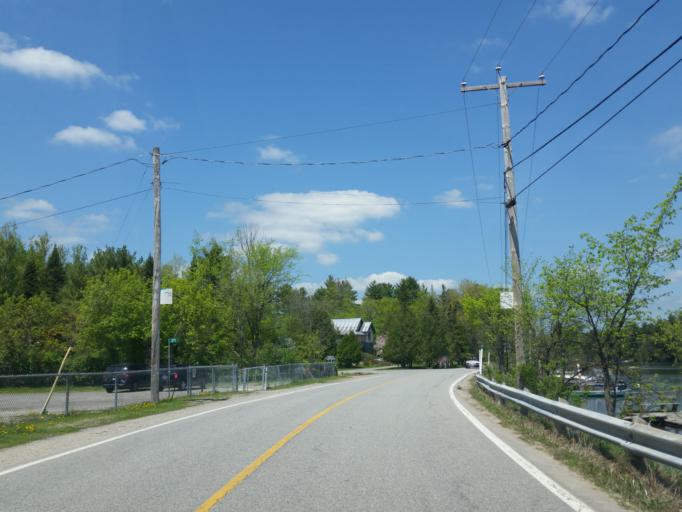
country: CA
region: Quebec
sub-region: Outaouais
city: Wakefield
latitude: 45.6032
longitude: -75.8892
